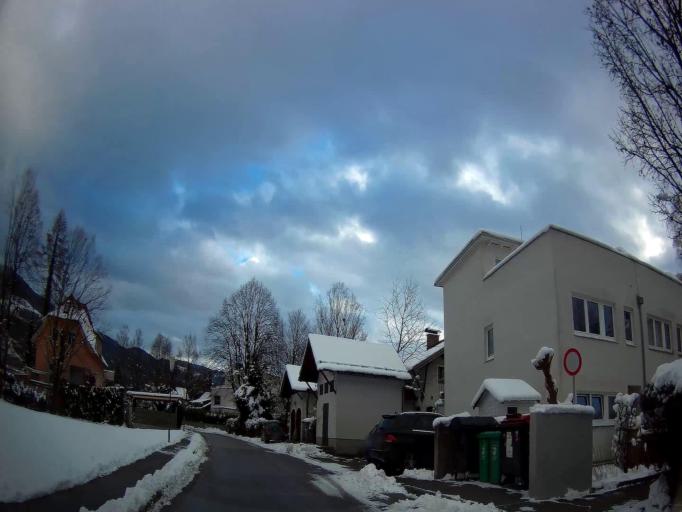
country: AT
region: Salzburg
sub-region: Salzburg Stadt
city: Salzburg
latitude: 47.7921
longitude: 13.0773
